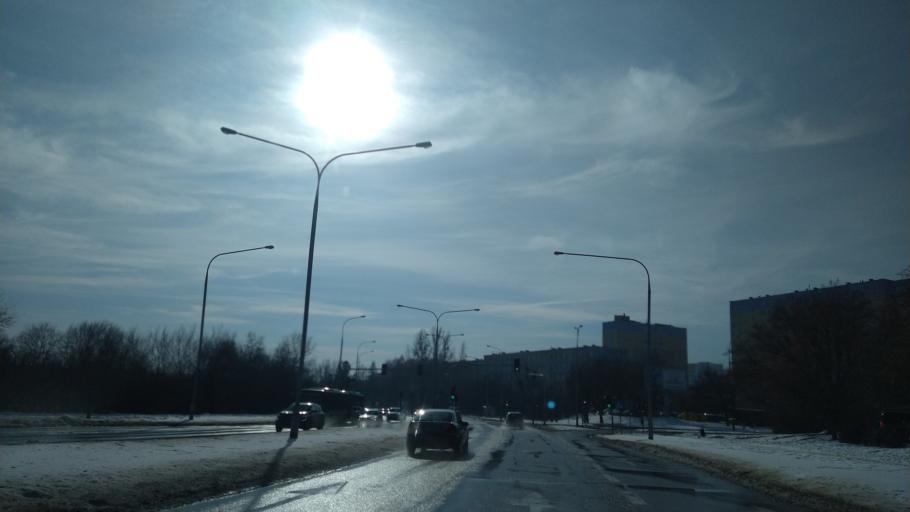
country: PL
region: Warmian-Masurian Voivodeship
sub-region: Powiat olsztynski
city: Olsztyn
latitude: 53.7543
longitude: 20.5034
